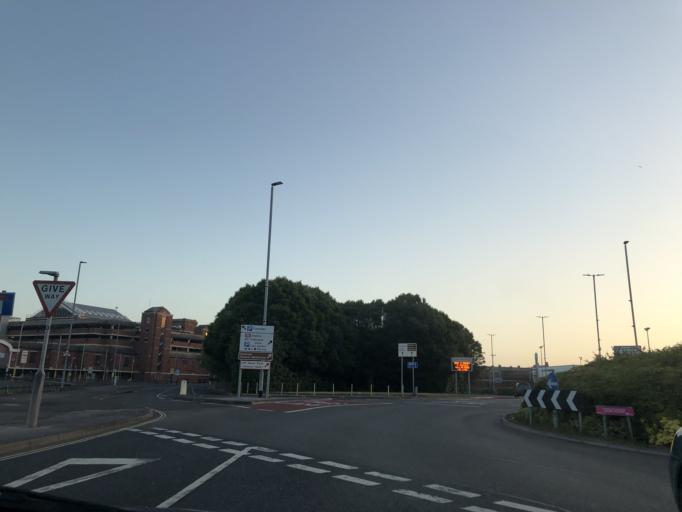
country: GB
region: England
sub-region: Portsmouth
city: Portsmouth
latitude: 50.8031
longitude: -1.0900
